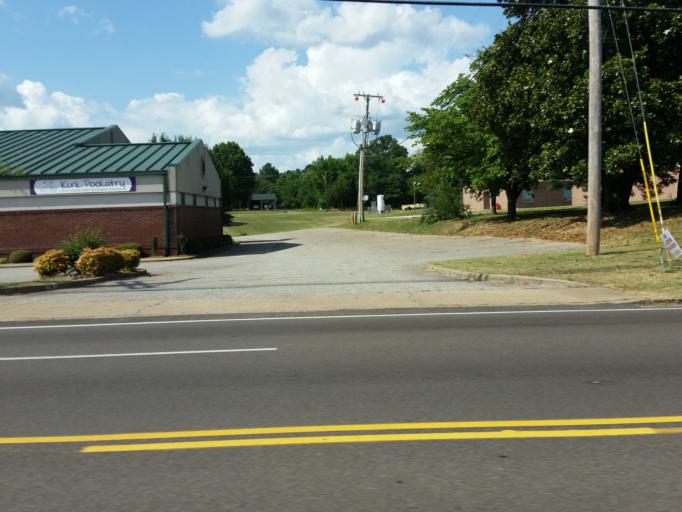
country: US
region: Tennessee
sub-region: Henderson County
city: Lexington
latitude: 35.6544
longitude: -88.3999
